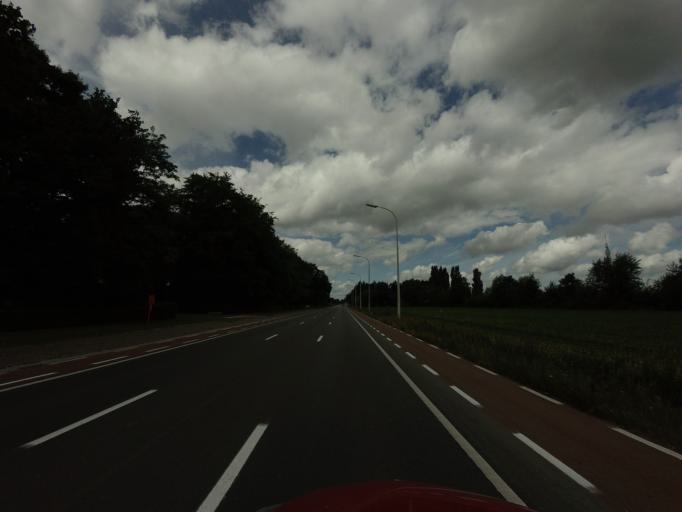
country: BE
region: Flanders
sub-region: Provincie Oost-Vlaanderen
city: Sint-Laureins
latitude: 51.2028
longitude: 3.5059
